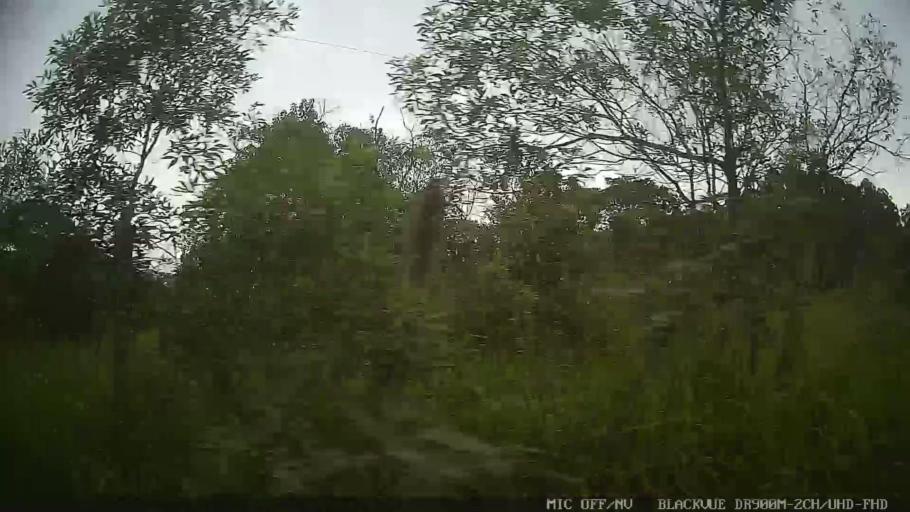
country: BR
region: Sao Paulo
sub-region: Atibaia
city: Atibaia
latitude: -23.1768
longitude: -46.5807
